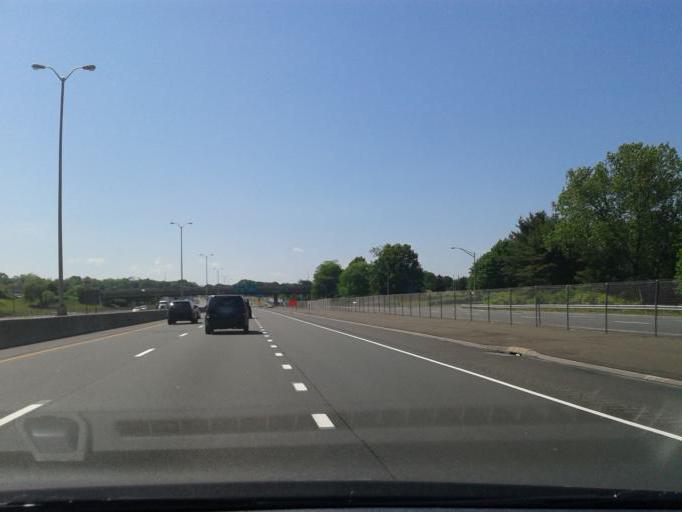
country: US
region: Connecticut
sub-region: New London County
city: New London
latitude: 41.3676
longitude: -72.1122
